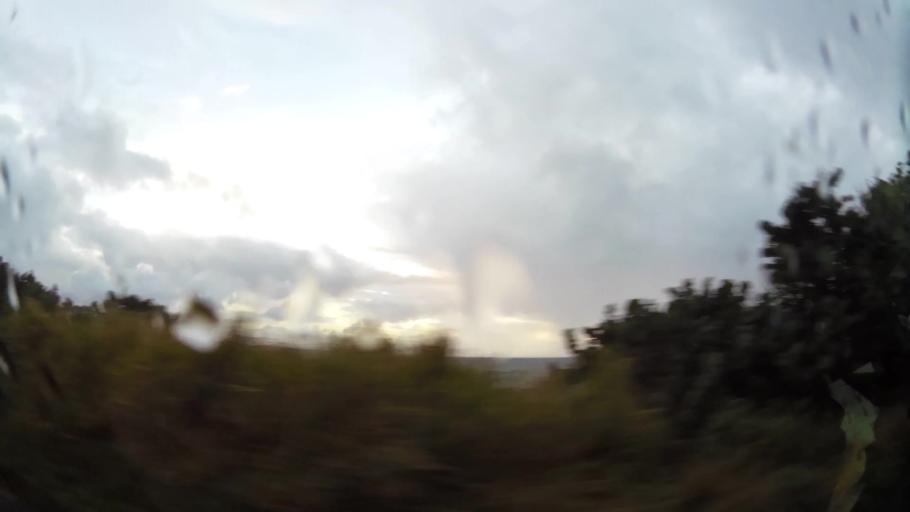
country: DM
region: Saint Andrew
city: Marigot
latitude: 15.5514
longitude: -61.2953
